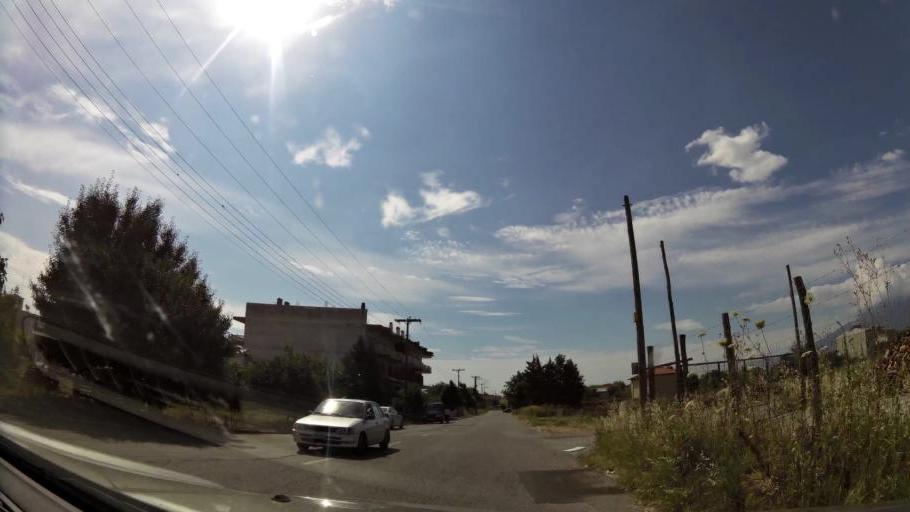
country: GR
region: Central Macedonia
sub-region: Nomos Pierias
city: Katerini
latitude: 40.2795
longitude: 22.4895
